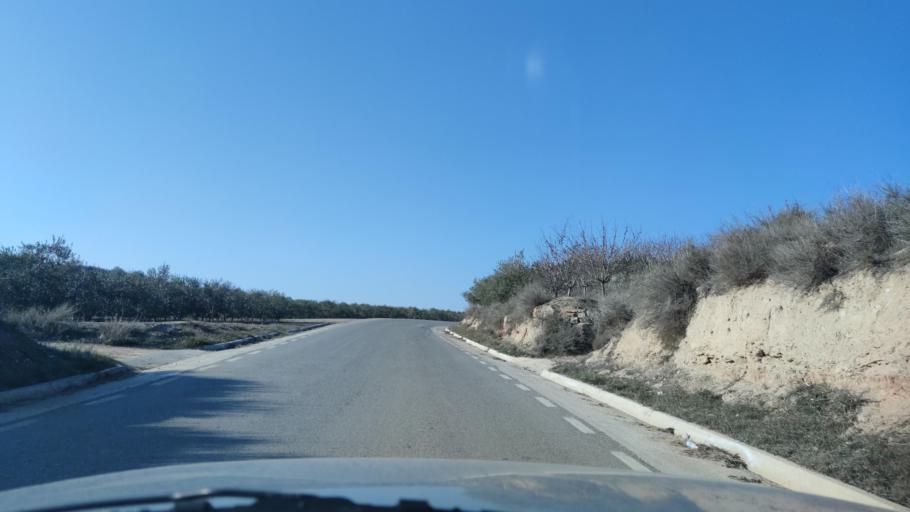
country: ES
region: Catalonia
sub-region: Provincia de Lleida
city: Torrebesses
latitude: 41.4662
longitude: 0.5655
